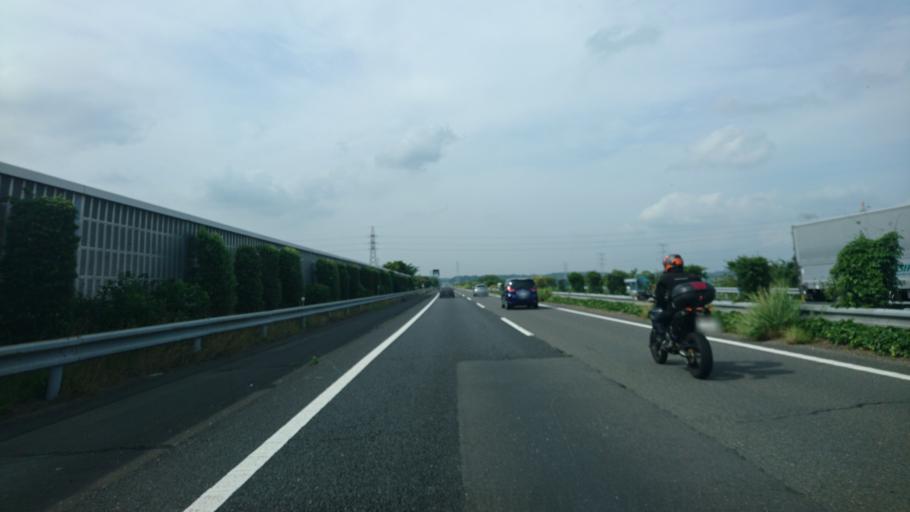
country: JP
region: Chiba
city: Kisarazu
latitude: 35.3960
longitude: 140.0050
